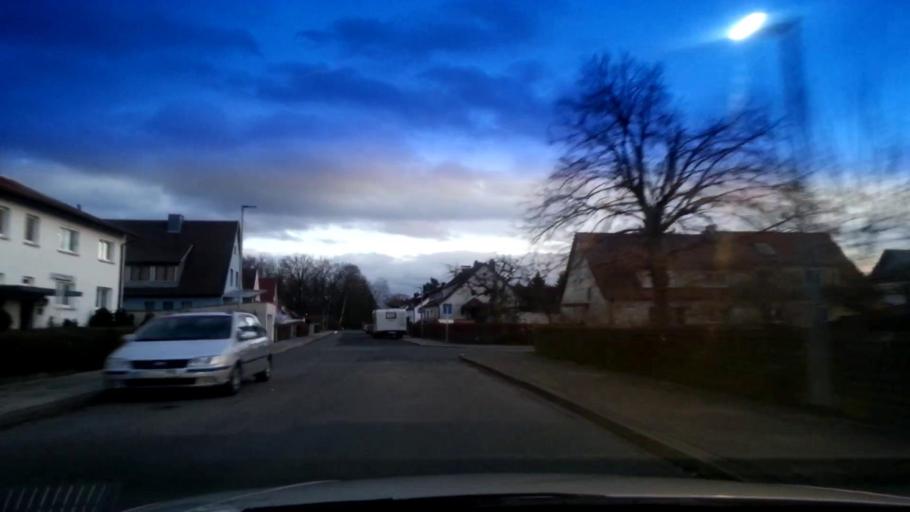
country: DE
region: Bavaria
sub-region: Upper Franconia
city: Gundelsheim
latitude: 49.9132
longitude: 10.9272
